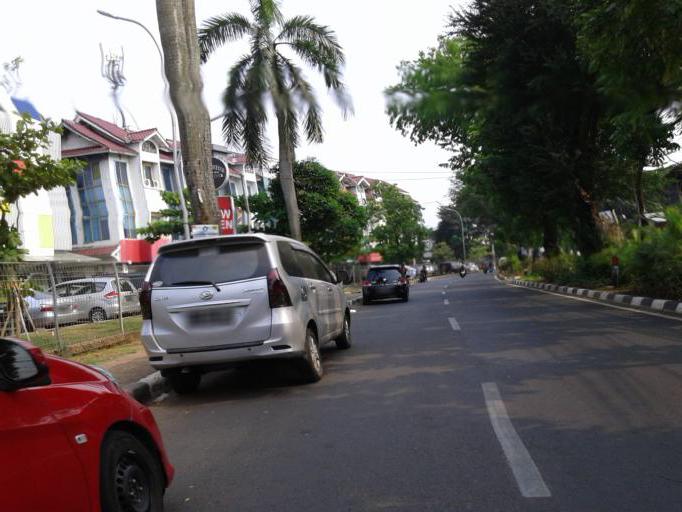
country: ID
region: West Java
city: Pamulang
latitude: -6.3053
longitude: 106.7819
